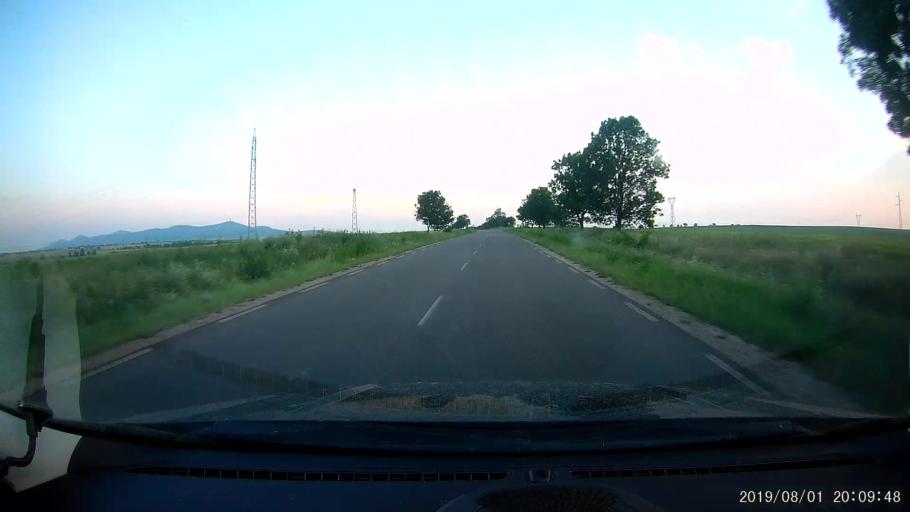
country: BG
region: Yambol
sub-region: Obshtina Yambol
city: Yambol
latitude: 42.4924
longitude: 26.5943
